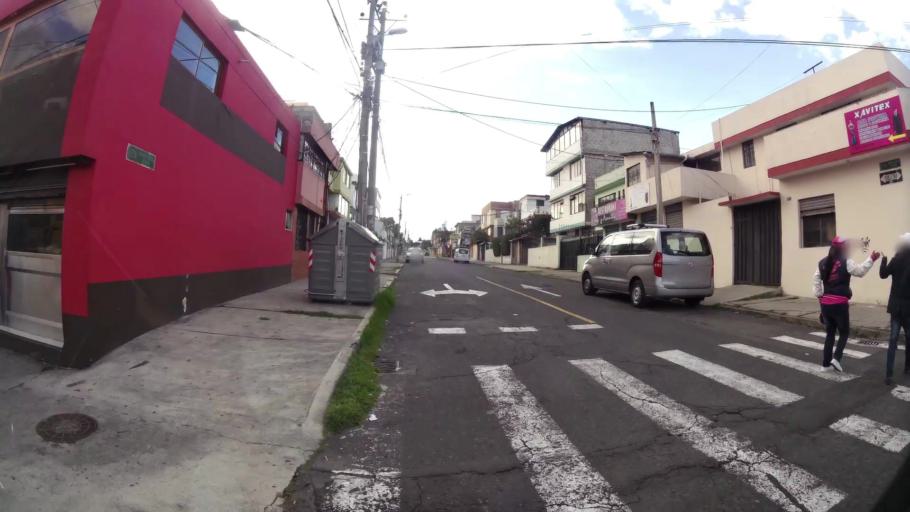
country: EC
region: Pichincha
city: Quito
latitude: -0.1400
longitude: -78.4759
